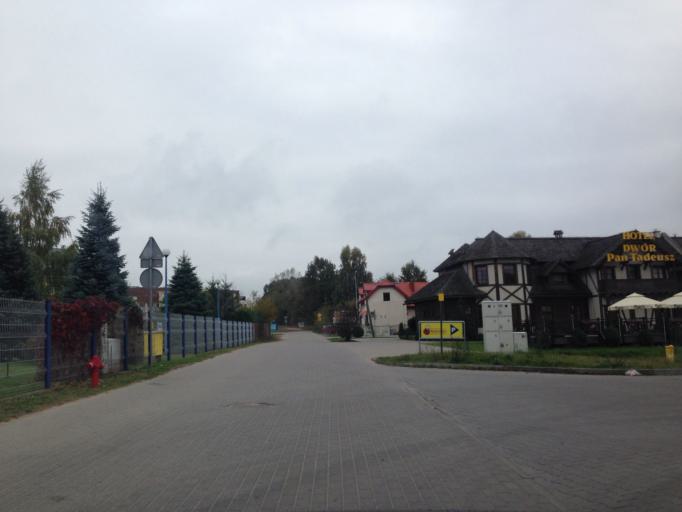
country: PL
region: Kujawsko-Pomorskie
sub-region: Powiat bydgoski
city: Osielsko
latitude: 53.1780
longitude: 18.0609
